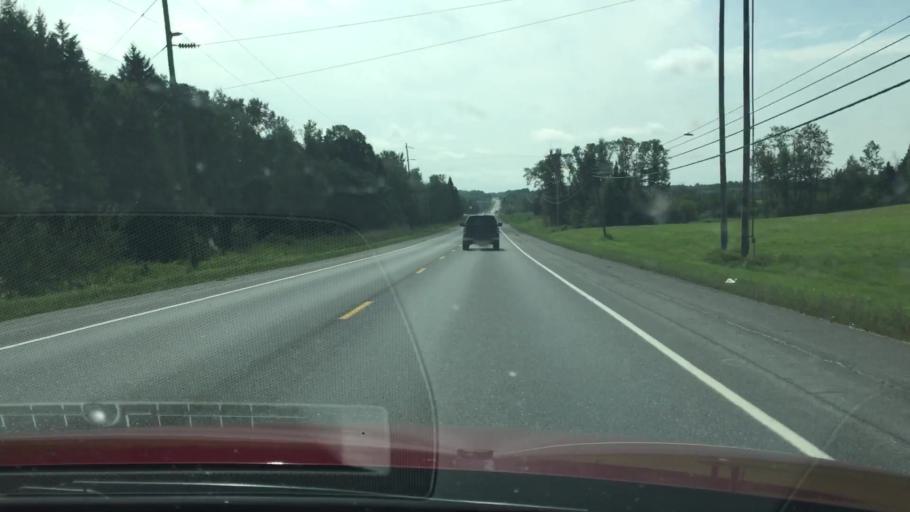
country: US
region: Maine
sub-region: Aroostook County
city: Easton
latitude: 46.4869
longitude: -67.8684
